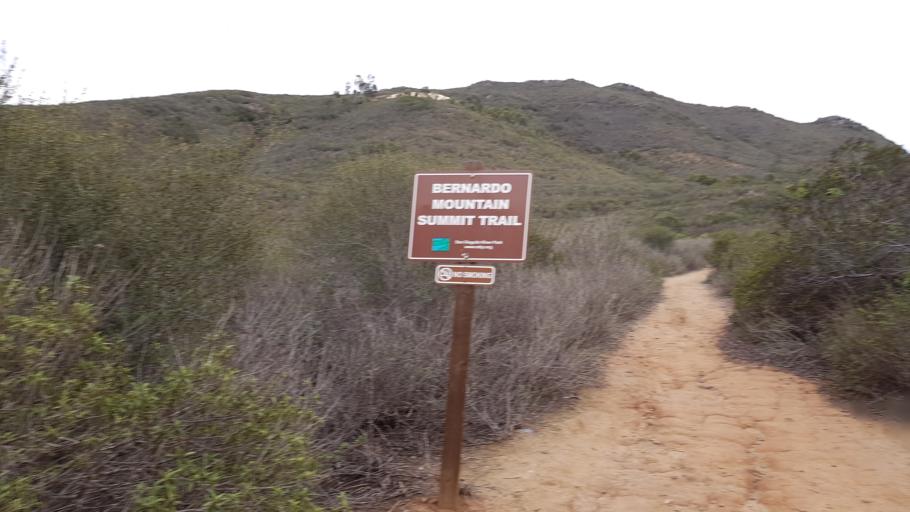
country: US
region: California
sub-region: San Diego County
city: Escondido
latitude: 33.0699
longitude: -117.0881
